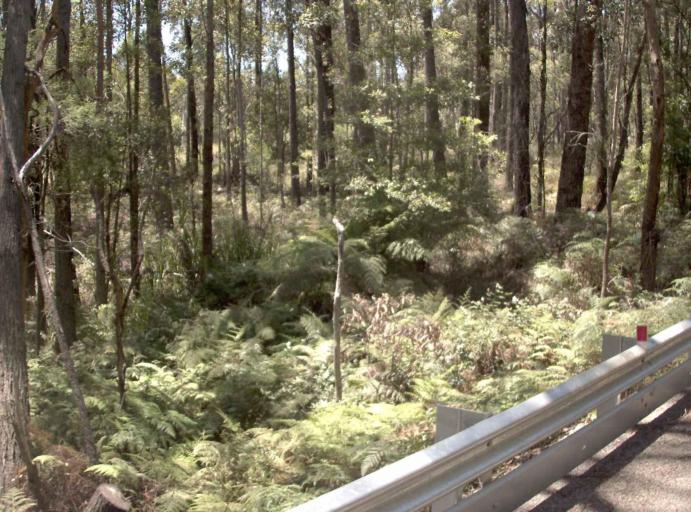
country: AU
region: Victoria
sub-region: East Gippsland
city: Lakes Entrance
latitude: -37.7027
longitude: 148.5806
